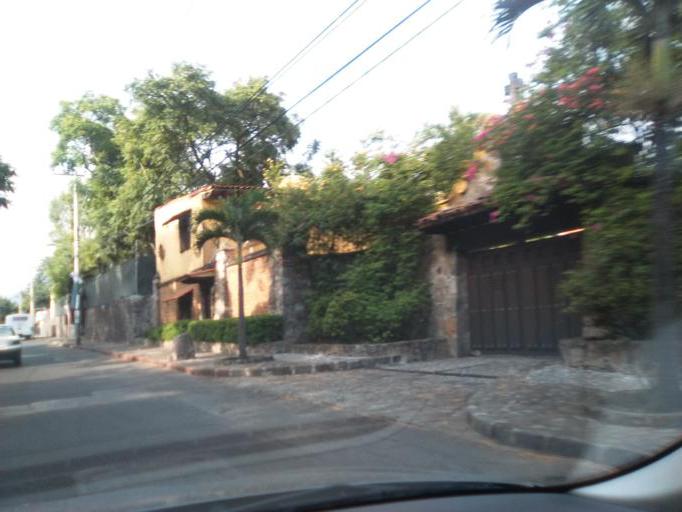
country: MX
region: Morelos
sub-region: Cuernavaca
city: Cuernavaca
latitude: 18.9045
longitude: -99.2271
